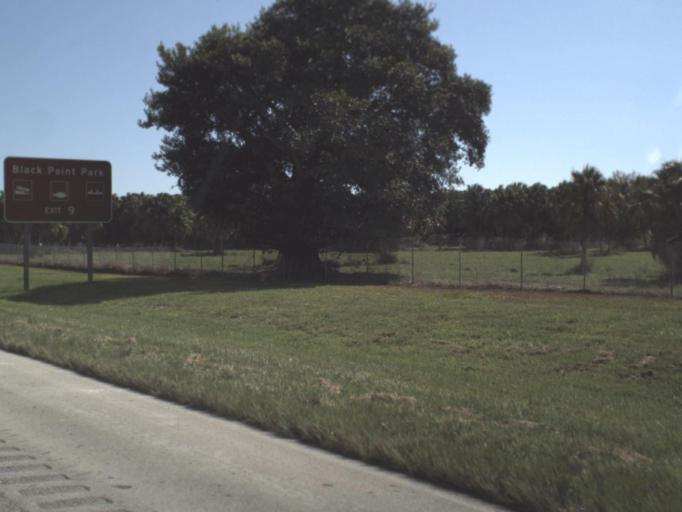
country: US
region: Florida
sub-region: Miami-Dade County
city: Princeton
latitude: 25.5301
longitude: -80.3831
